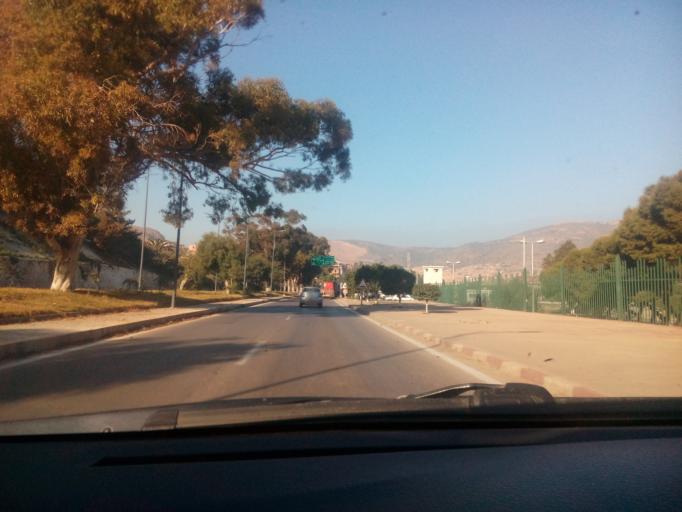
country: DZ
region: Oran
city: Mers el Kebir
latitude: 35.7166
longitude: -0.6949
